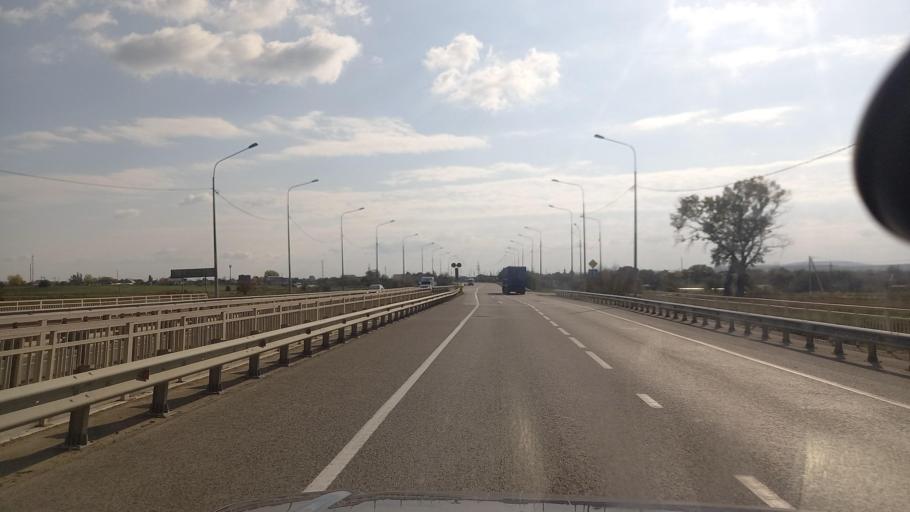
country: RU
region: Krasnodarskiy
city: Novoukrainskiy
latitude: 44.9008
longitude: 38.0376
